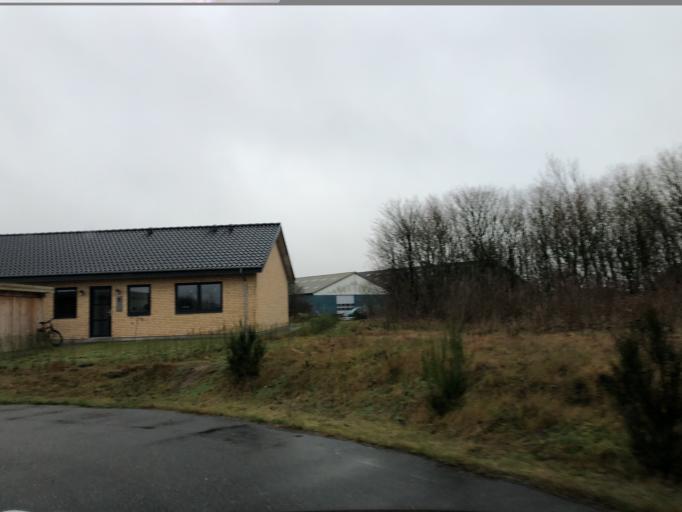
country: DK
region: Central Jutland
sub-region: Holstebro Kommune
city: Ulfborg
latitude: 56.1997
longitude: 8.3038
